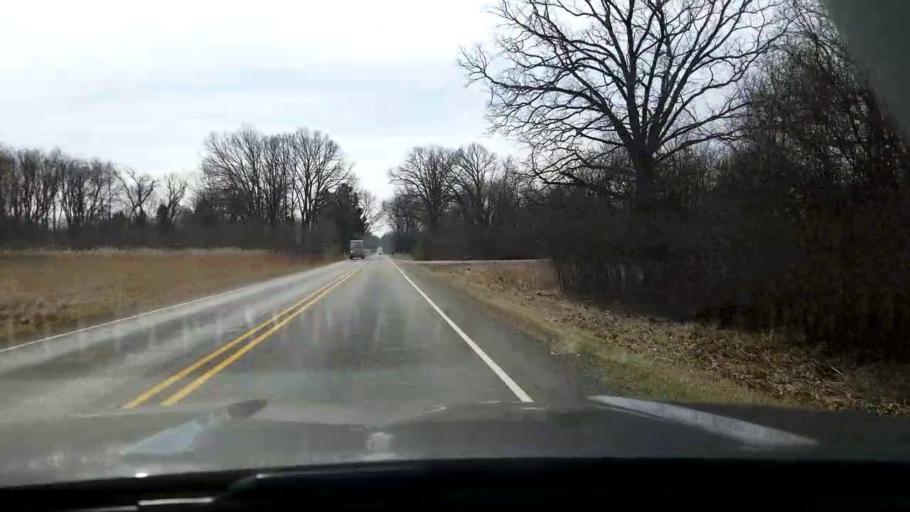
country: US
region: Michigan
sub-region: Jackson County
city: Spring Arbor
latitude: 42.2009
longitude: -84.5210
